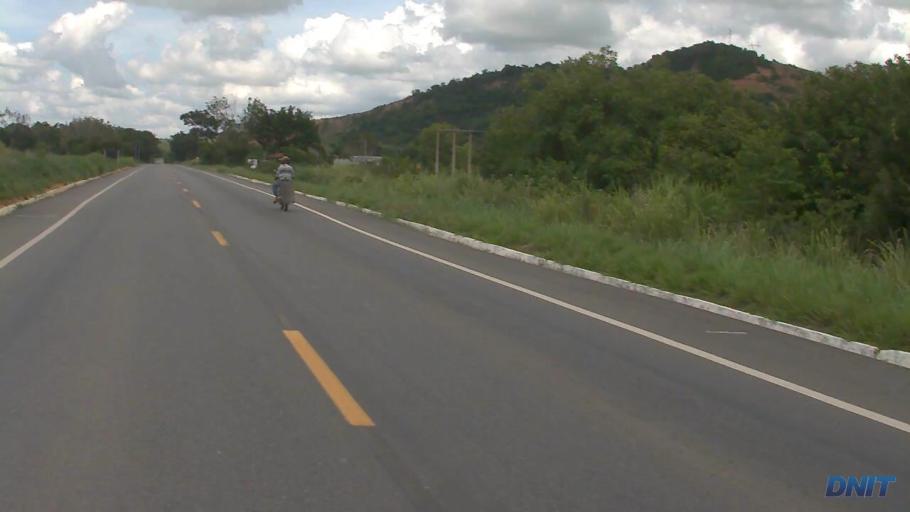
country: BR
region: Minas Gerais
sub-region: Governador Valadares
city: Governador Valadares
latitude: -18.9458
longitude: -42.0664
